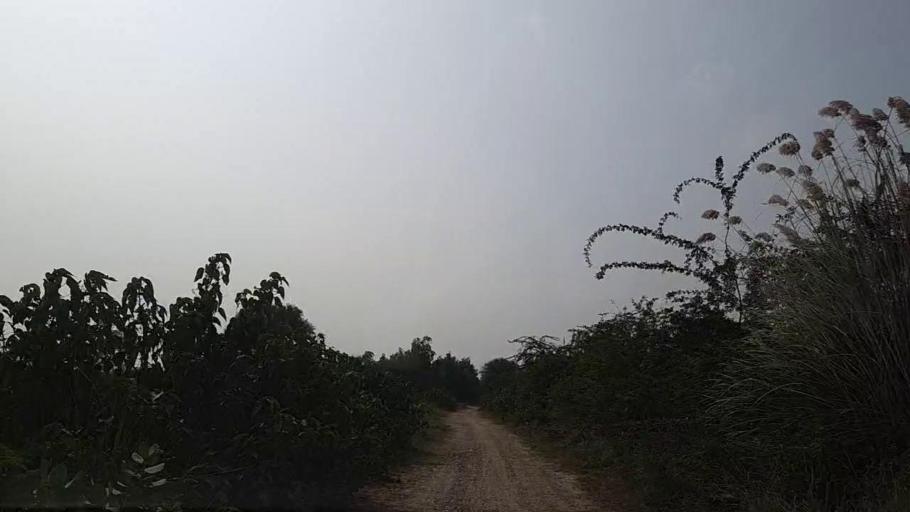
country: PK
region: Sindh
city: Mirpur Sakro
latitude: 24.6546
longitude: 67.7686
